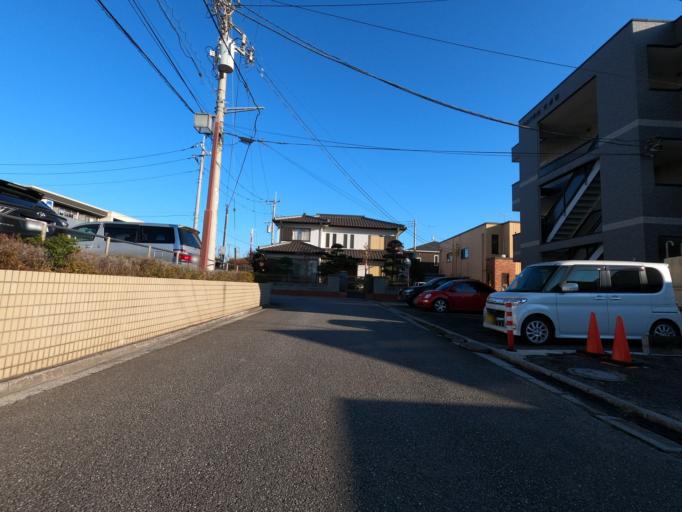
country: JP
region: Ibaraki
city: Moriya
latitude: 35.9333
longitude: 140.0010
